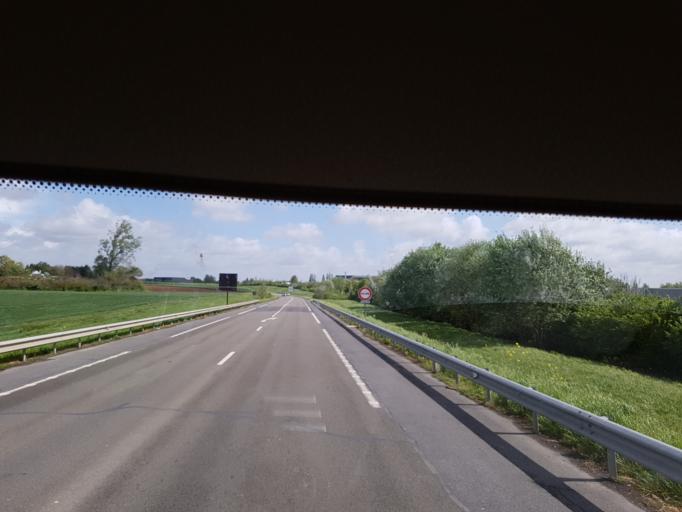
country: FR
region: Nord-Pas-de-Calais
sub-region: Departement du Nord
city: Proville
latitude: 50.1701
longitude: 3.1923
